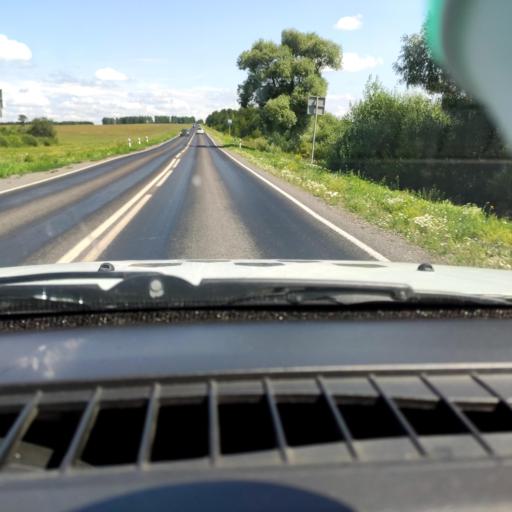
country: RU
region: Bashkortostan
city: Verkhniye Kigi
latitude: 55.4590
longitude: 58.4324
